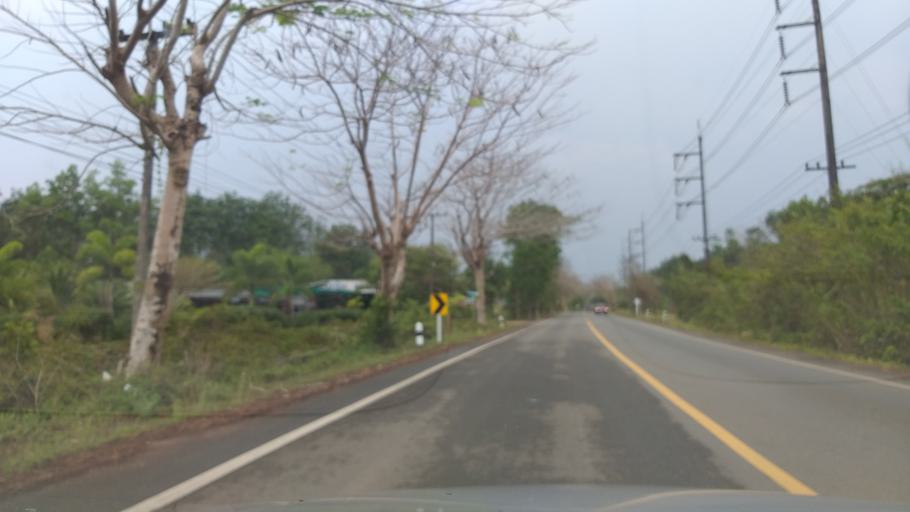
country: TH
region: Trat
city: Laem Ngop
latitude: 12.2758
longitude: 102.3057
